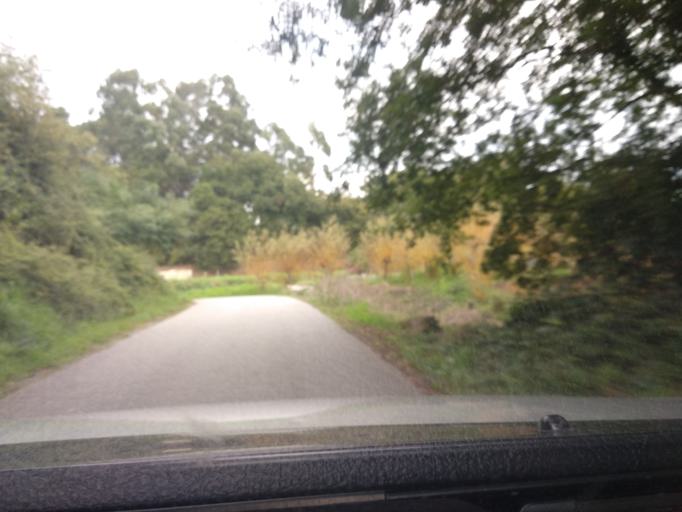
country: ES
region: Galicia
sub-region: Provincia de Pontevedra
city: Moana
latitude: 42.2952
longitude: -8.7350
